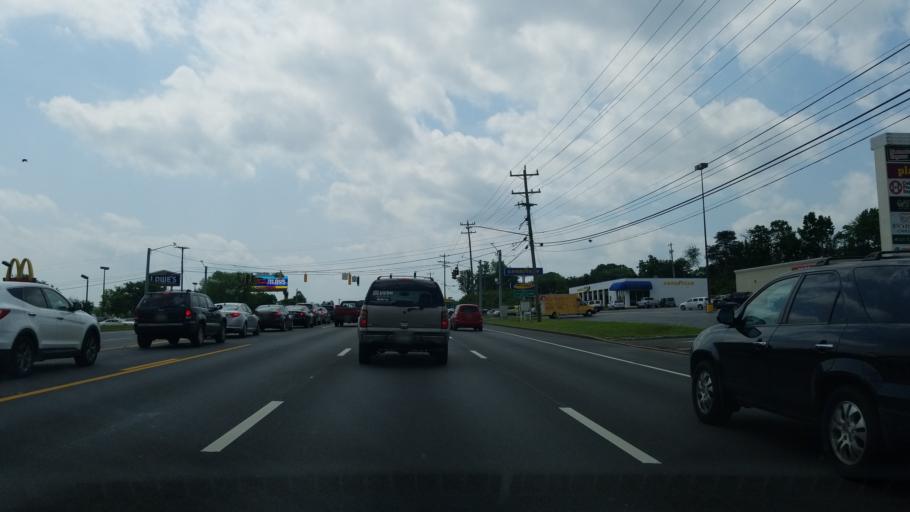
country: US
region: Tennessee
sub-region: Hamilton County
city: Red Bank
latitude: 35.1391
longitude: -85.2481
